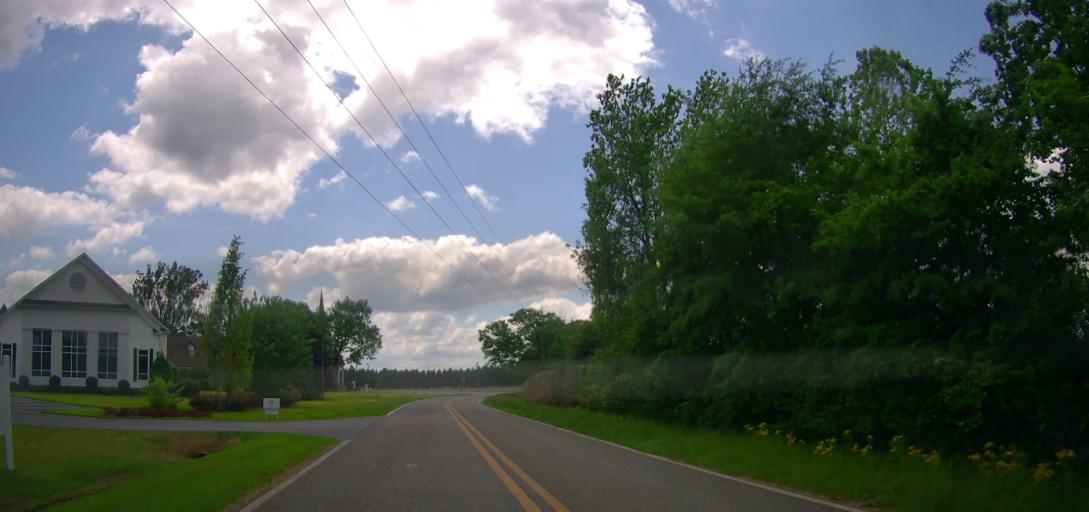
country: US
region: Georgia
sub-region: Laurens County
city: Dublin
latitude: 32.5991
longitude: -82.9260
